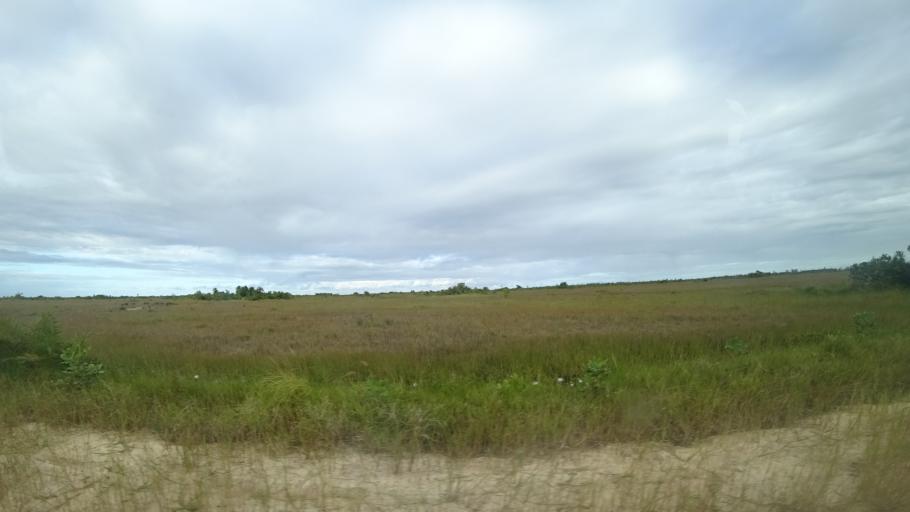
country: MZ
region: Sofala
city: Beira
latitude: -19.6974
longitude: 35.0313
